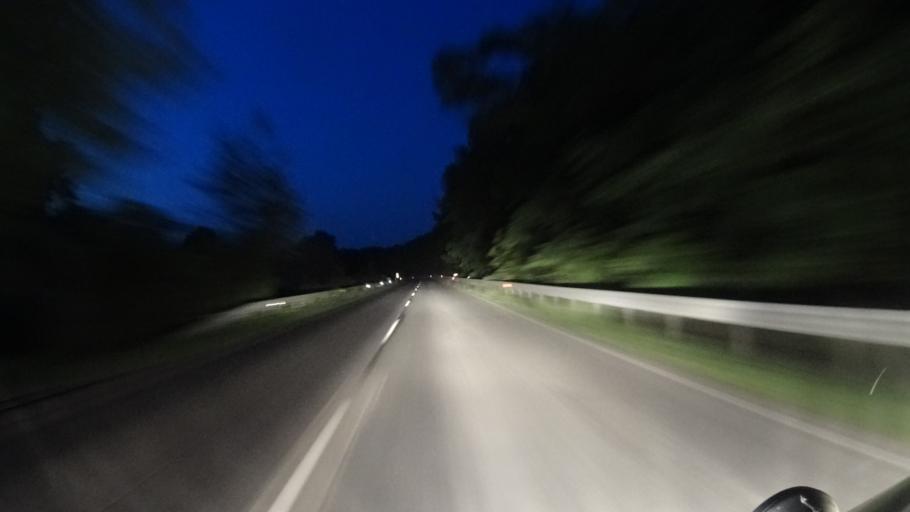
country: HU
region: Somogy
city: Balatonbereny
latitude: 46.6888
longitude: 17.3519
